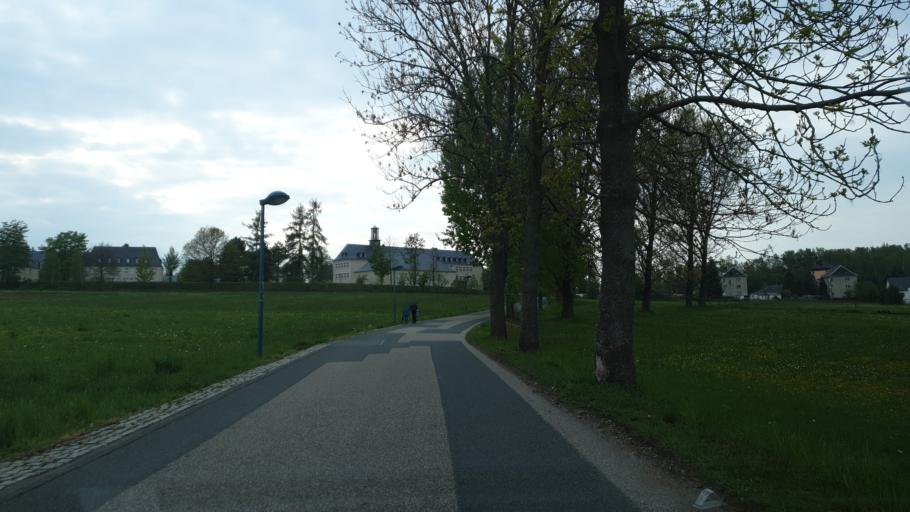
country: DE
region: Saxony
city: Oelsnitz
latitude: 50.7333
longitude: 12.7104
